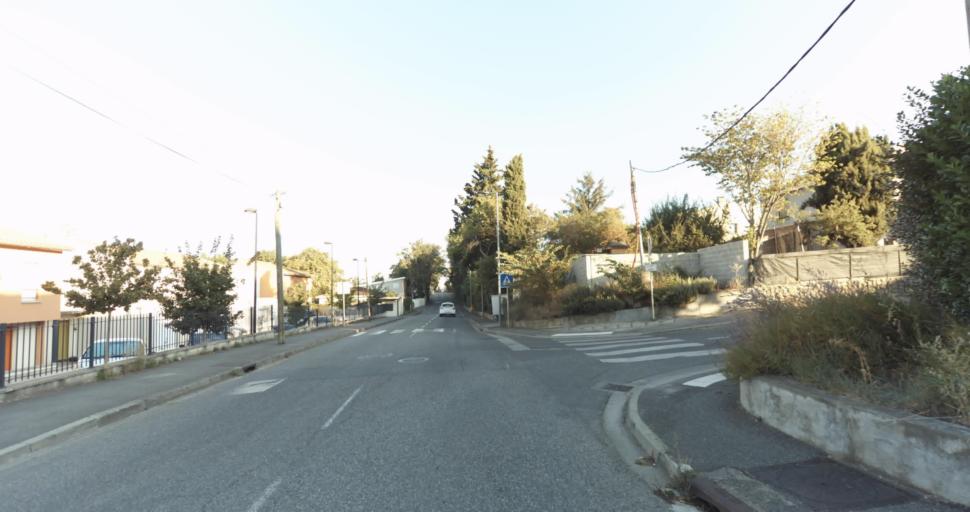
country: FR
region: Midi-Pyrenees
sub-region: Departement de la Haute-Garonne
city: L'Union
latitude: 43.6591
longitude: 1.4797
